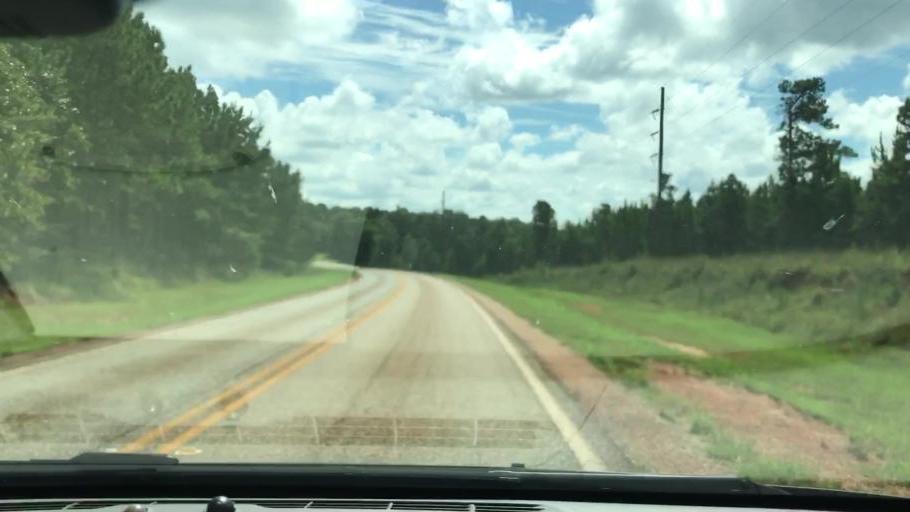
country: US
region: Georgia
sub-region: Stewart County
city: Lumpkin
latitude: 32.0643
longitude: -84.8370
